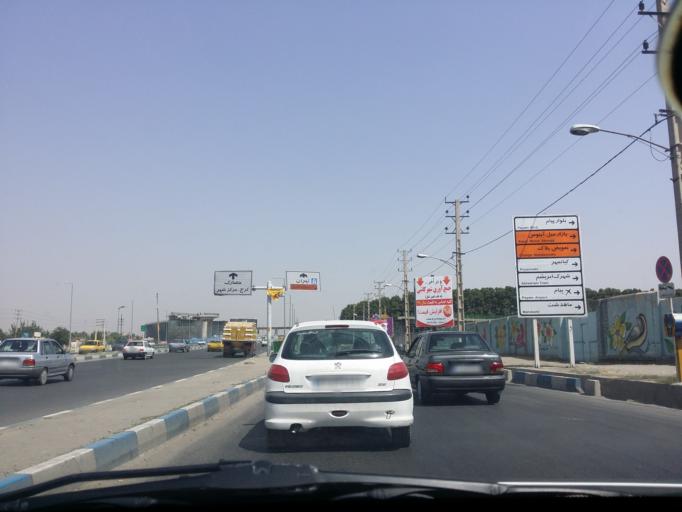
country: IR
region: Alborz
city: Karaj
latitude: 35.8524
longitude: 50.9018
